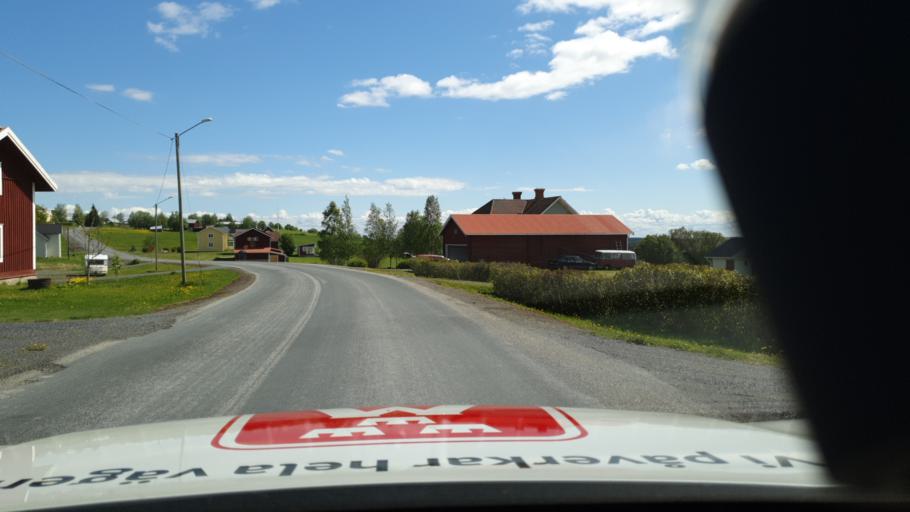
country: SE
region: Jaemtland
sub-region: Krokoms Kommun
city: Valla
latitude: 63.3034
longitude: 13.8709
